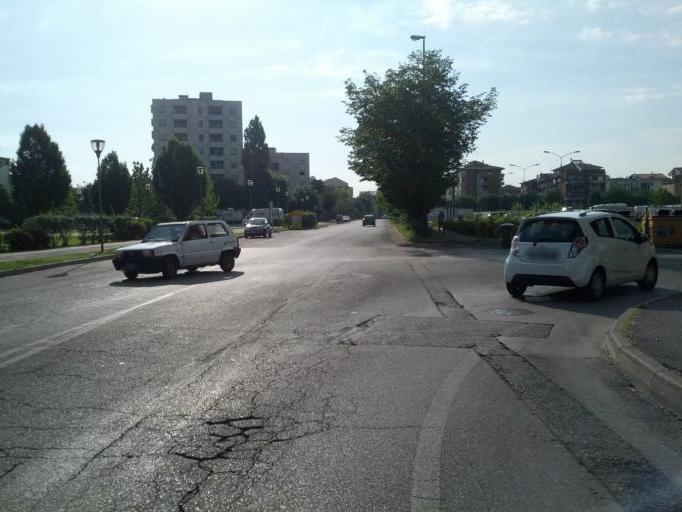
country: IT
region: Veneto
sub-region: Provincia di Verona
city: Montorio
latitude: 45.4334
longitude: 11.0519
